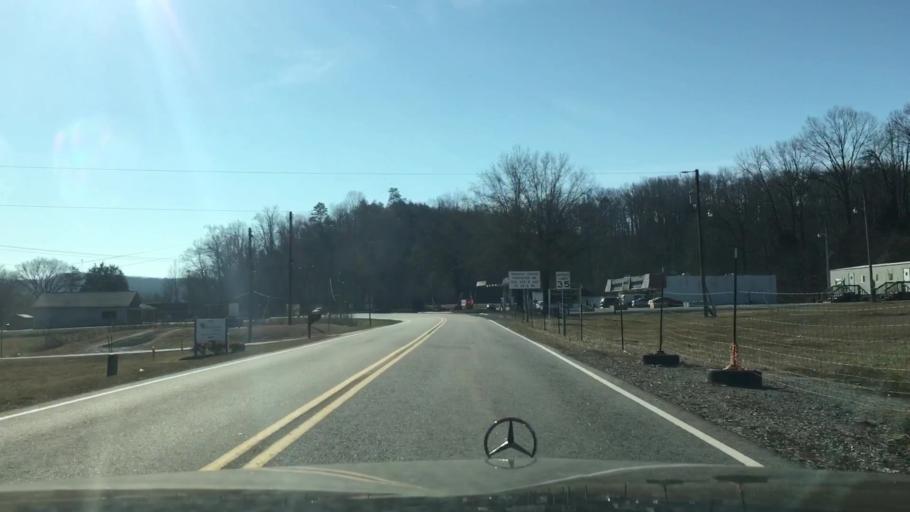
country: US
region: Virginia
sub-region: Campbell County
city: Altavista
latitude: 37.1046
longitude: -79.2854
